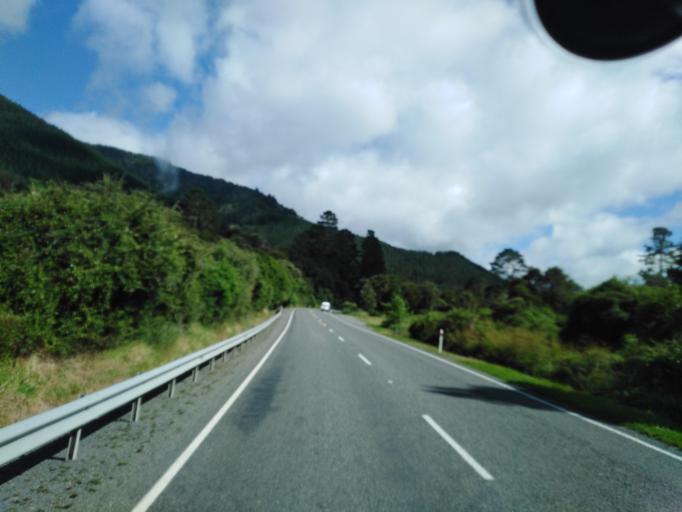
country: NZ
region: Nelson
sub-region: Nelson City
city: Nelson
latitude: -41.2916
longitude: 173.5730
